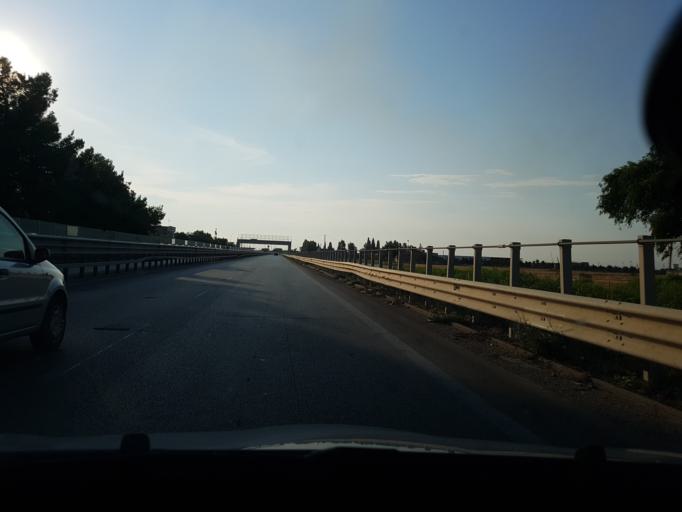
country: IT
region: Apulia
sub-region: Provincia di Foggia
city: Carapelle
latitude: 41.3659
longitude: 15.6980
